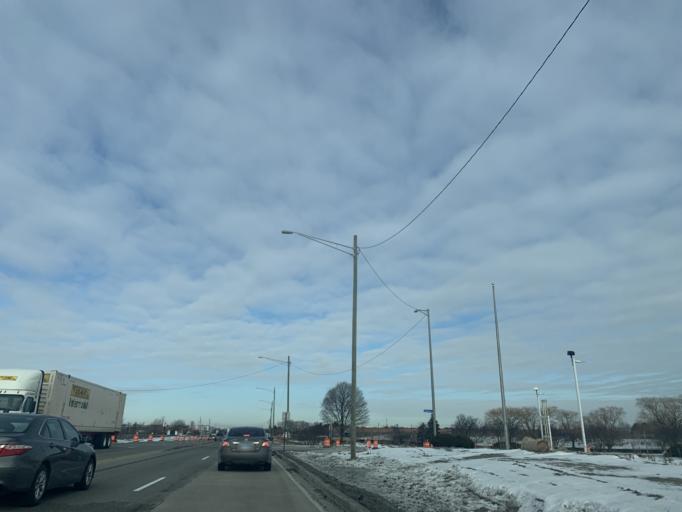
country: US
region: Illinois
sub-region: Will County
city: Romeoville
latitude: 41.6582
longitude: -88.1249
